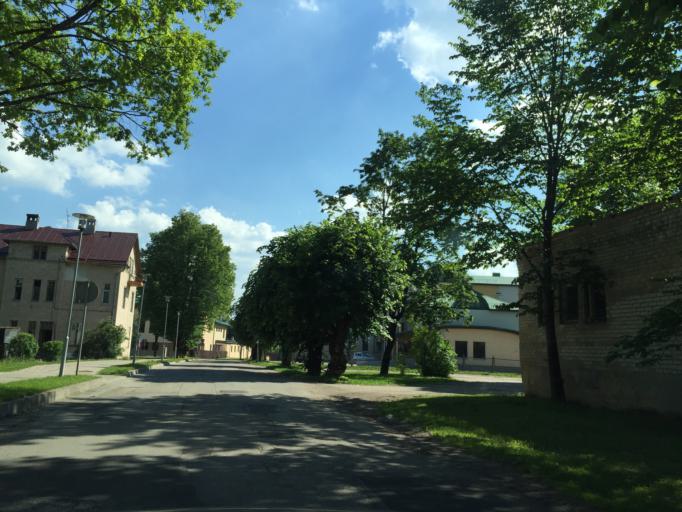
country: LV
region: Sigulda
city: Sigulda
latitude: 57.1578
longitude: 24.8447
